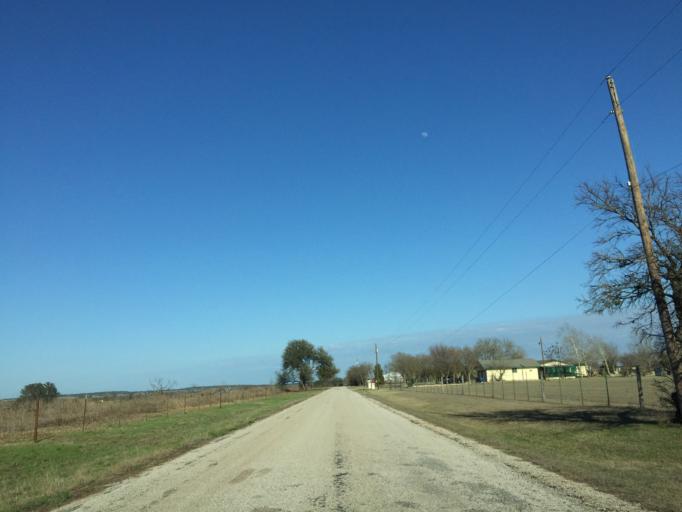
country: US
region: Texas
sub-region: Williamson County
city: Florence
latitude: 30.7747
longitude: -97.8479
